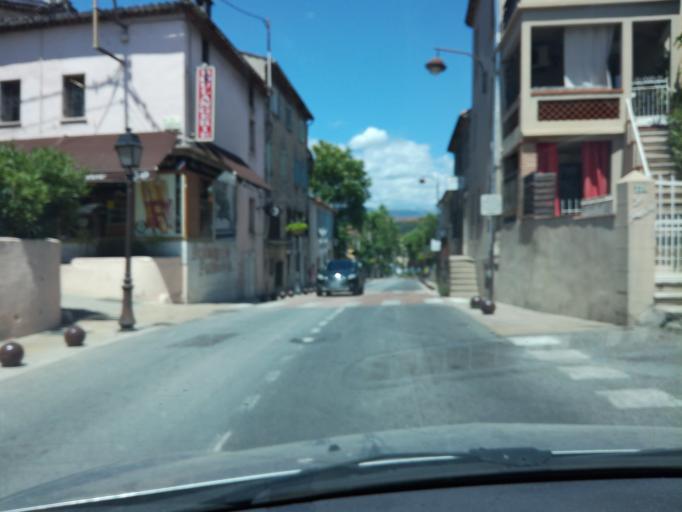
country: FR
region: Provence-Alpes-Cote d'Azur
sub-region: Departement des Alpes-Maritimes
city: Mougins
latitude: 43.5989
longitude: 6.9862
